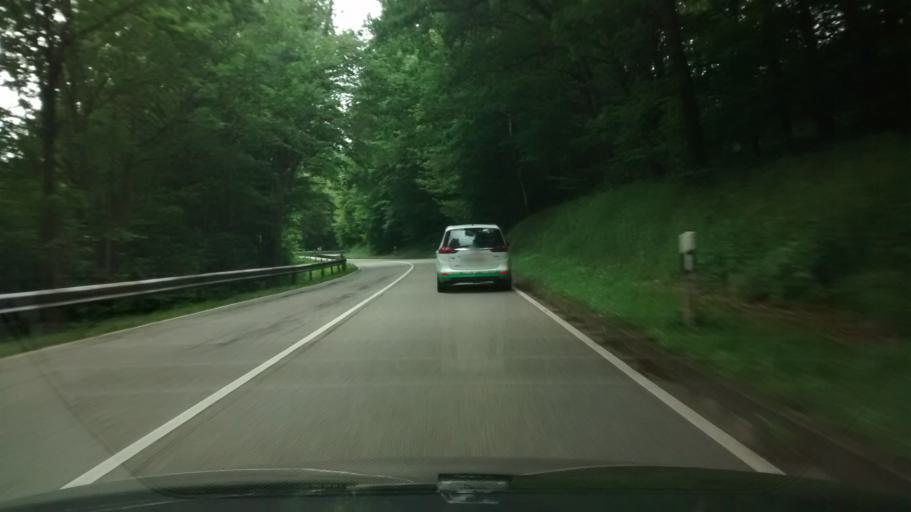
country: DE
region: Rheinland-Pfalz
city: Vorderweidenthal
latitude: 49.1167
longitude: 7.8604
